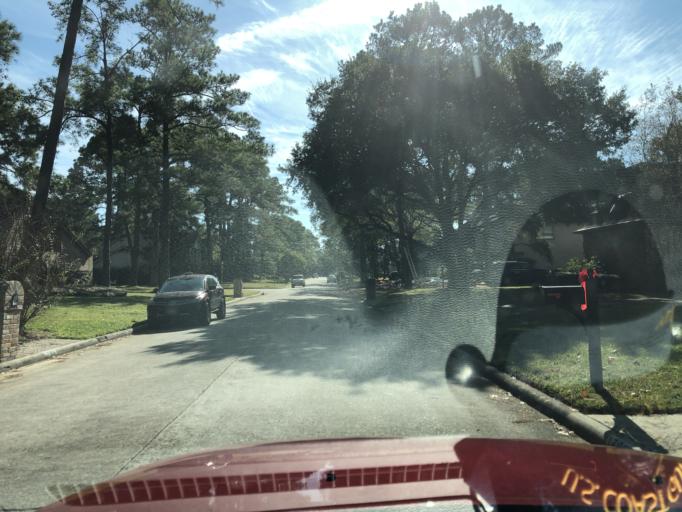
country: US
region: Texas
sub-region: Harris County
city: Tomball
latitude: 30.0240
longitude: -95.5521
